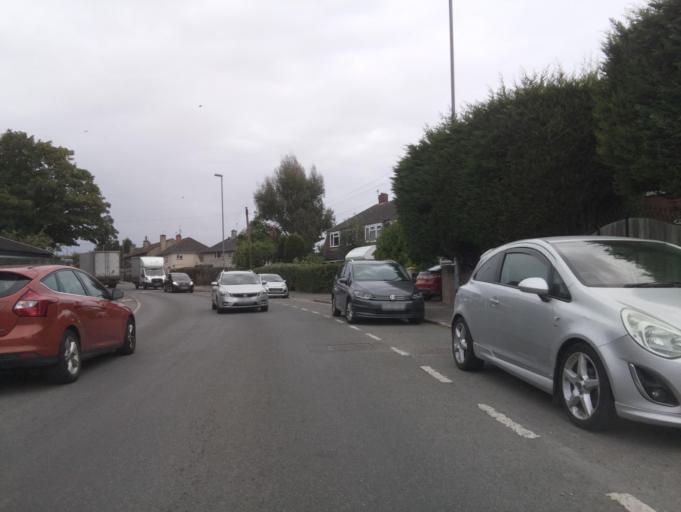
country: GB
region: England
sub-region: South Gloucestershire
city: Severn Beach
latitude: 51.5125
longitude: -2.6289
